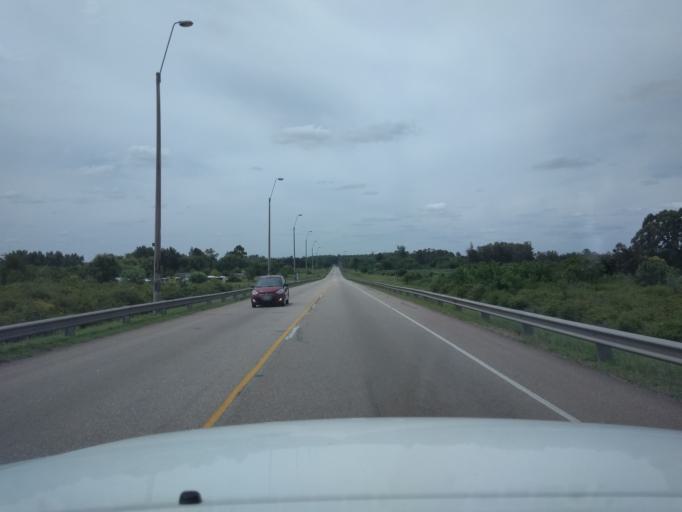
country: UY
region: Canelones
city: Canelones
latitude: -34.5419
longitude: -56.2741
